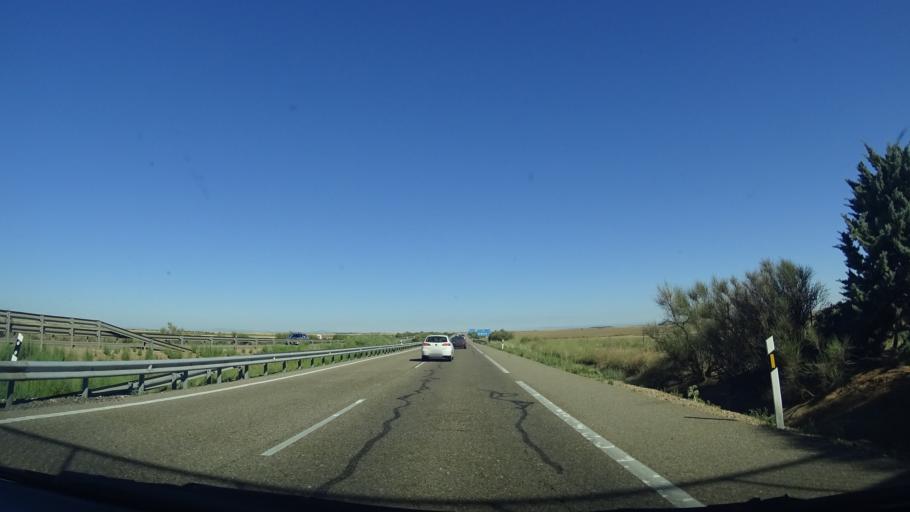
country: ES
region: Castille and Leon
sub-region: Provincia de Zamora
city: Villalpando
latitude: 41.8432
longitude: -5.3954
